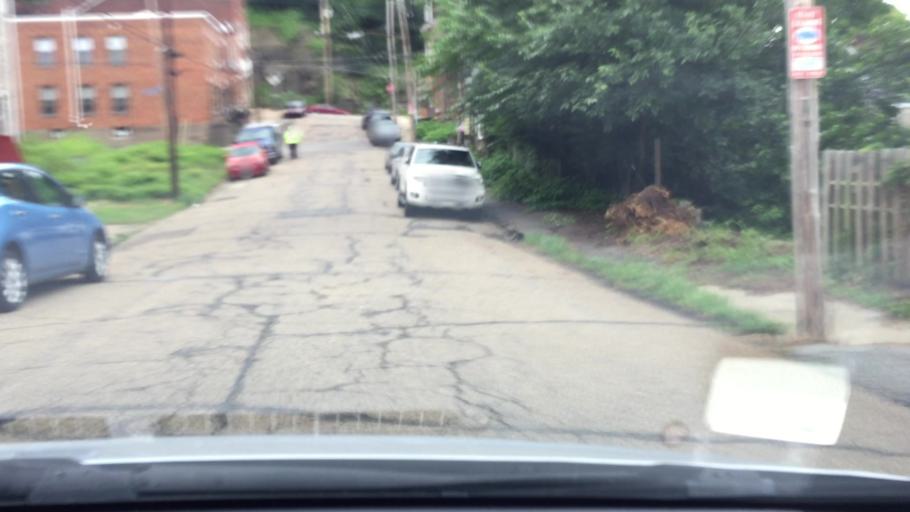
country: US
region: Pennsylvania
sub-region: Allegheny County
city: Pittsburgh
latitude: 40.4592
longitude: -80.0095
